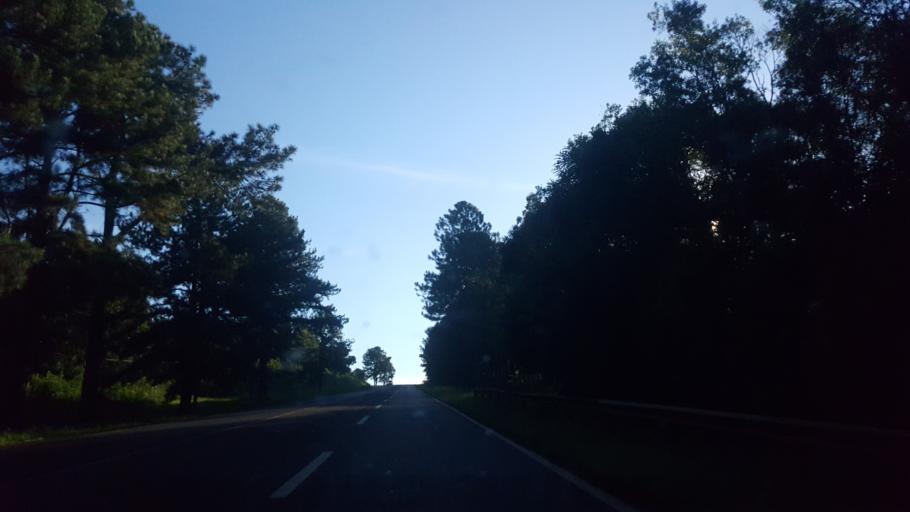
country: AR
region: Misiones
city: Caraguatay
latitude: -26.6663
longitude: -54.7609
